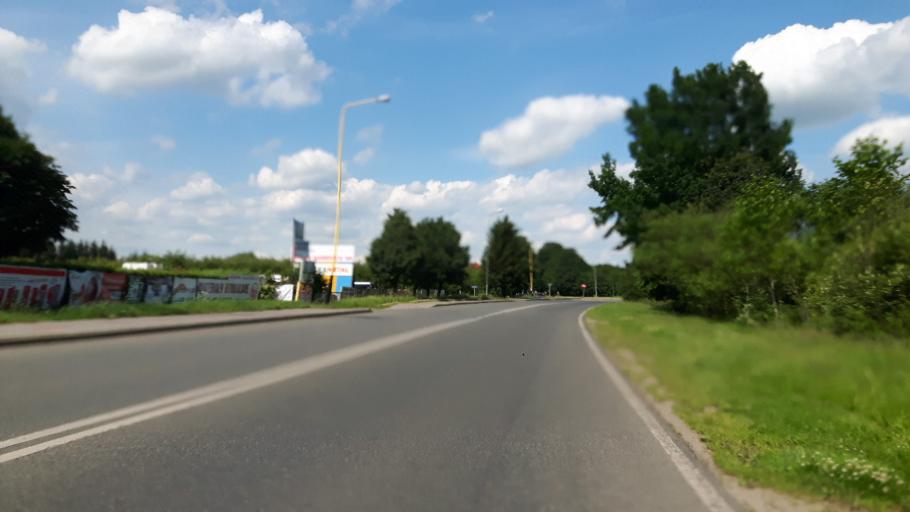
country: PL
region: West Pomeranian Voivodeship
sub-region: Powiat goleniowski
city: Nowogard
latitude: 53.6801
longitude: 15.1177
